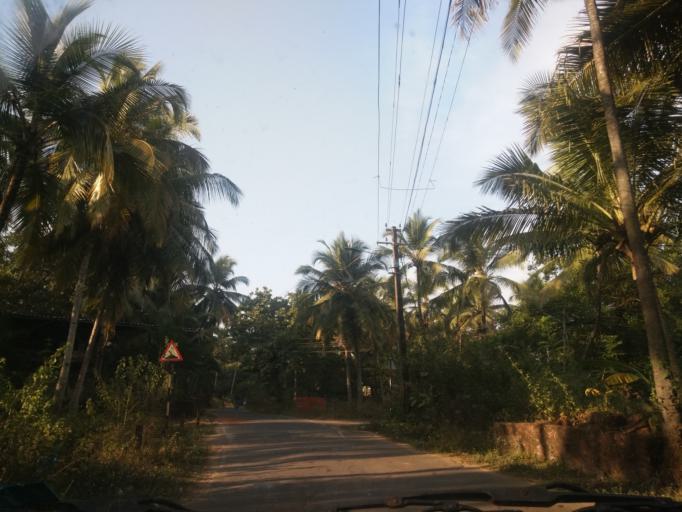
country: IN
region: Goa
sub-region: South Goa
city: Chinchinim
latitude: 15.2436
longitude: 73.9709
